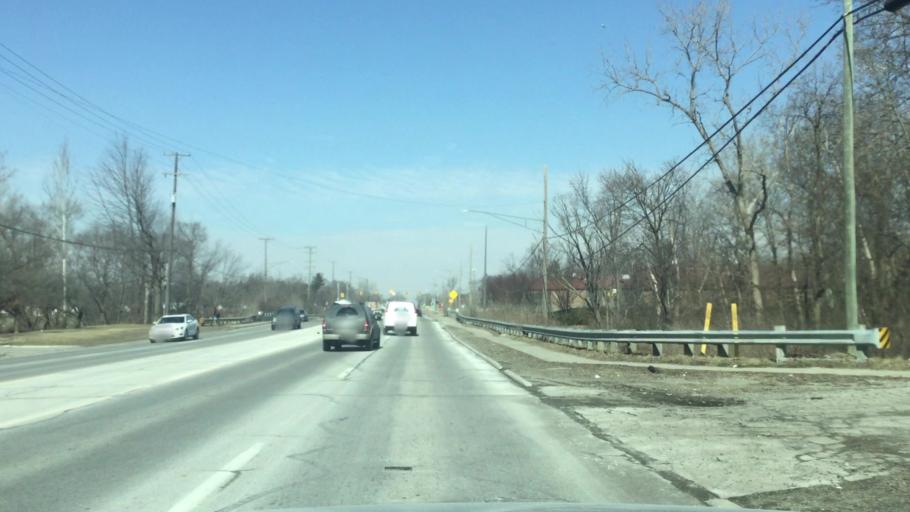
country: US
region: Michigan
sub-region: Wayne County
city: Inkster
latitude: 42.2964
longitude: -83.3101
